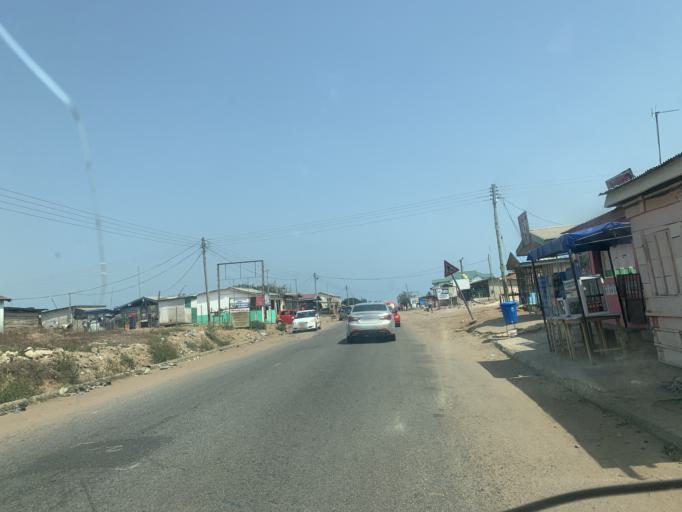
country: GH
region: Central
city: Winneba
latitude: 5.3979
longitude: -0.6496
